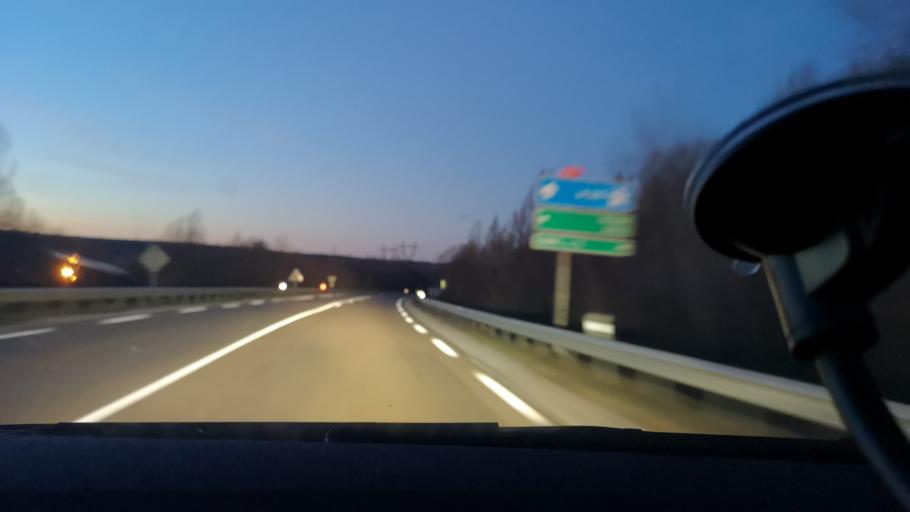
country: FR
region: Franche-Comte
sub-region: Departement du Jura
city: Champagnole
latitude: 46.7557
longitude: 5.9118
